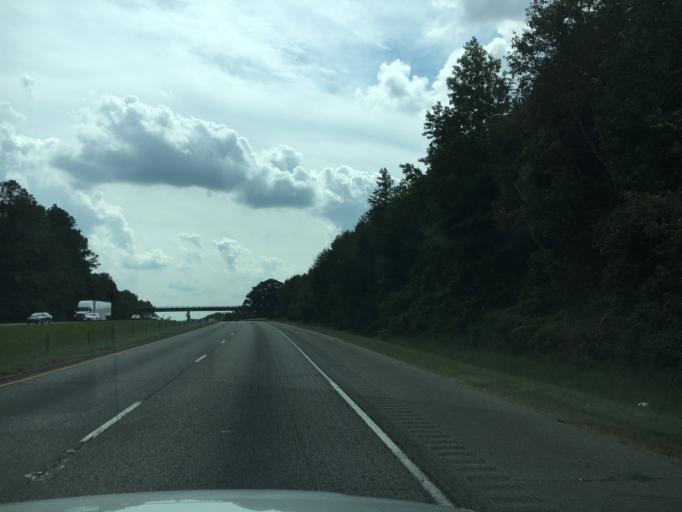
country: US
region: Georgia
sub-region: Franklin County
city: Carnesville
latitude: 34.3855
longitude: -83.2428
